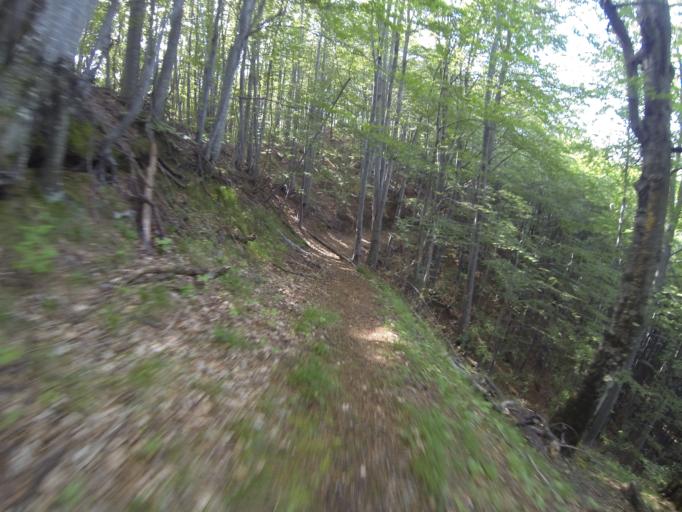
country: RO
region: Valcea
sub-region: Comuna Barbatesti
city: Barbatesti
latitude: 45.2498
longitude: 24.1590
